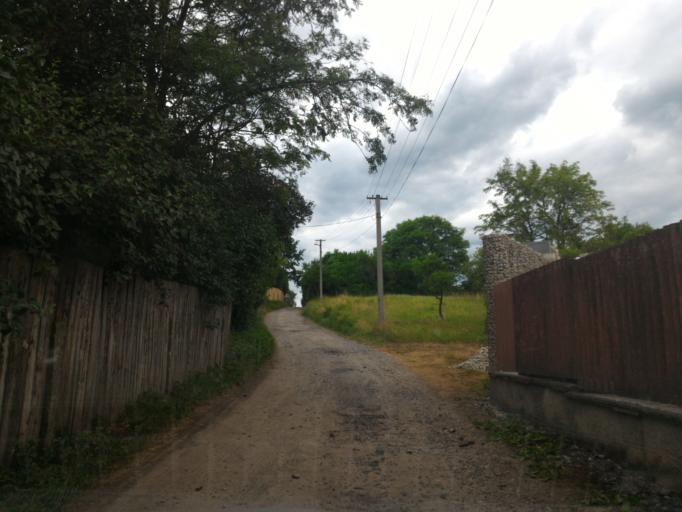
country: CZ
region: Vysocina
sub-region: Okres Jihlava
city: Telc
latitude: 49.1930
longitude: 15.4503
